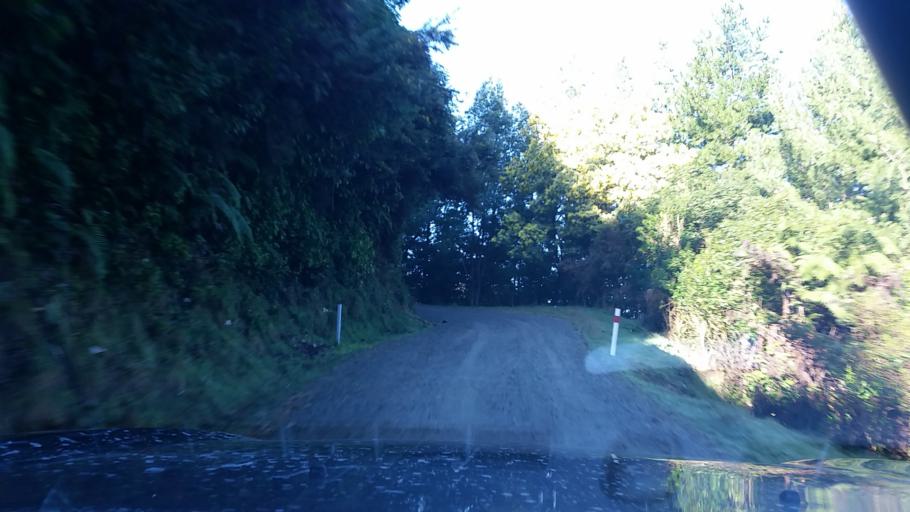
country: NZ
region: Marlborough
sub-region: Marlborough District
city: Picton
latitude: -41.1391
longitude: 174.0506
